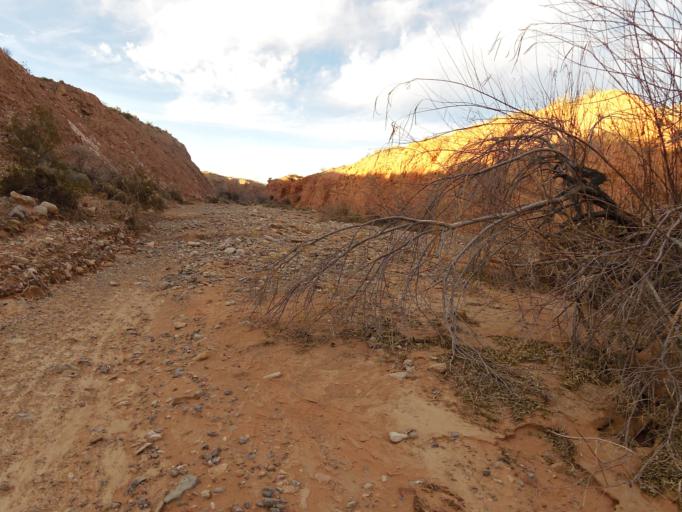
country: US
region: Nevada
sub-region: Clark County
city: Boulder City
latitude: 36.2423
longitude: -114.6323
